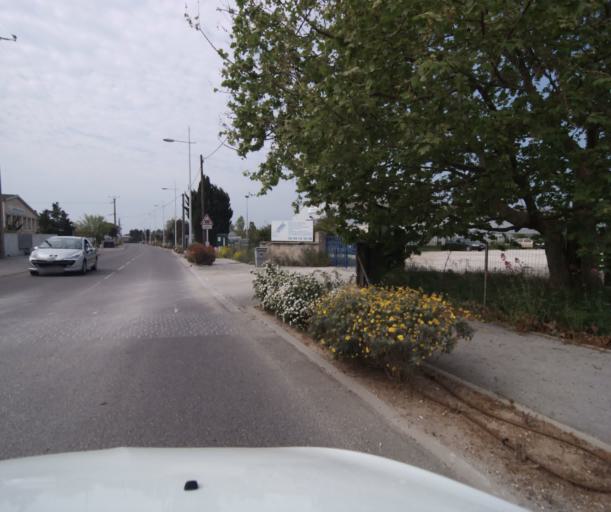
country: FR
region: Provence-Alpes-Cote d'Azur
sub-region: Departement du Var
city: La Farlede
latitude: 43.1457
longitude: 6.0367
